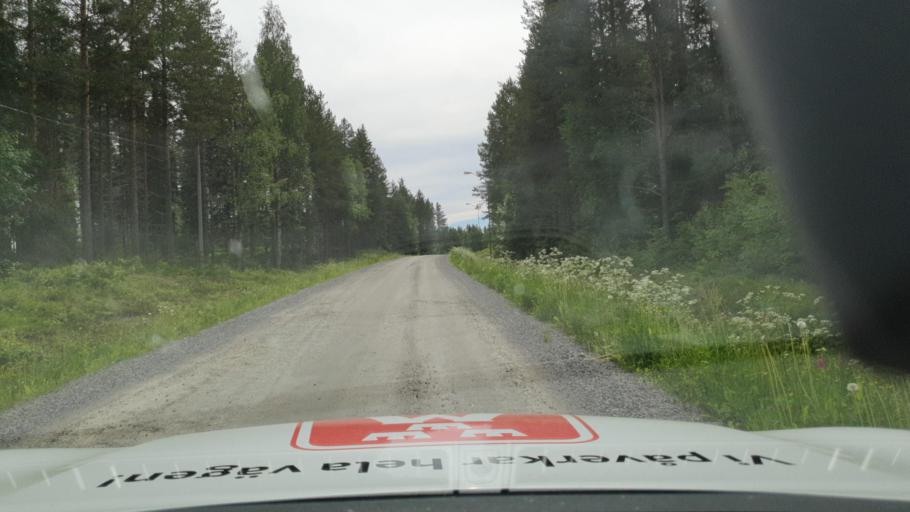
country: SE
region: Vaesterbotten
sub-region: Skelleftea Kommun
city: Burea
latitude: 64.4661
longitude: 21.0498
